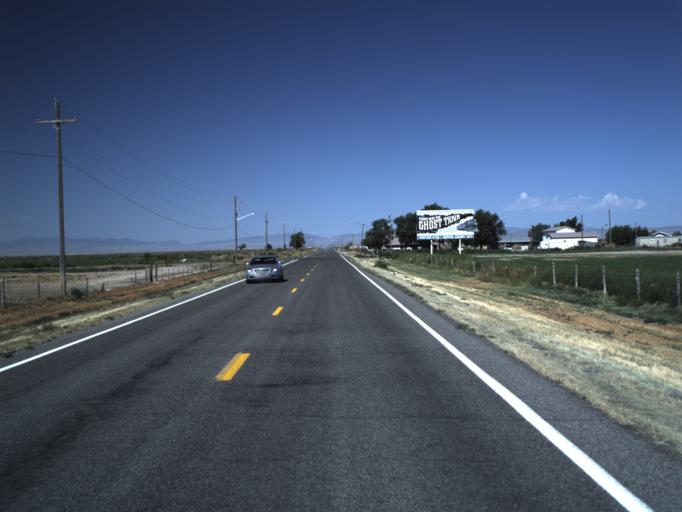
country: US
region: Utah
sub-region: Millard County
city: Delta
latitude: 39.3308
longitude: -112.6730
